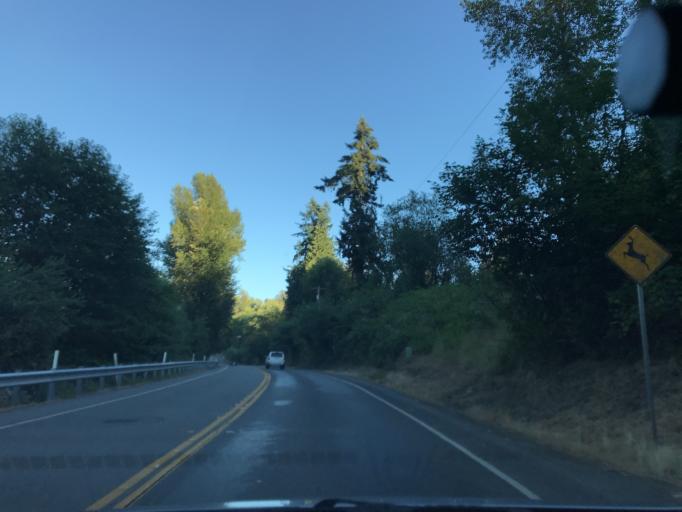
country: US
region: Washington
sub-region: King County
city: Auburn
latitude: 47.2702
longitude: -122.2062
